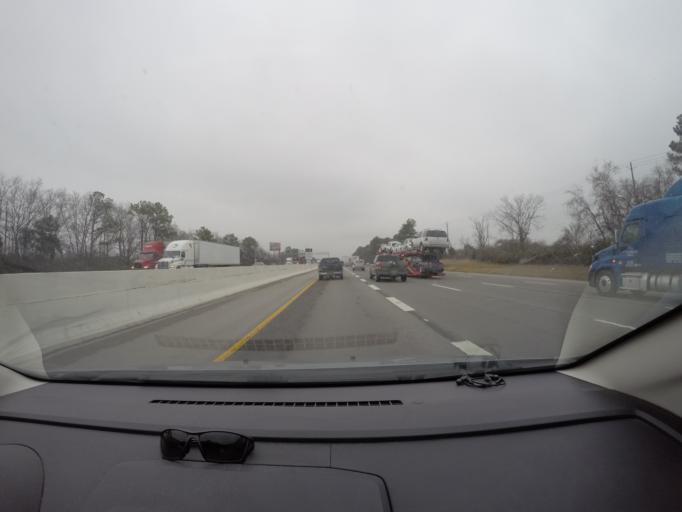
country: US
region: Tennessee
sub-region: Rutherford County
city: Murfreesboro
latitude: 35.8617
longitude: -86.4513
